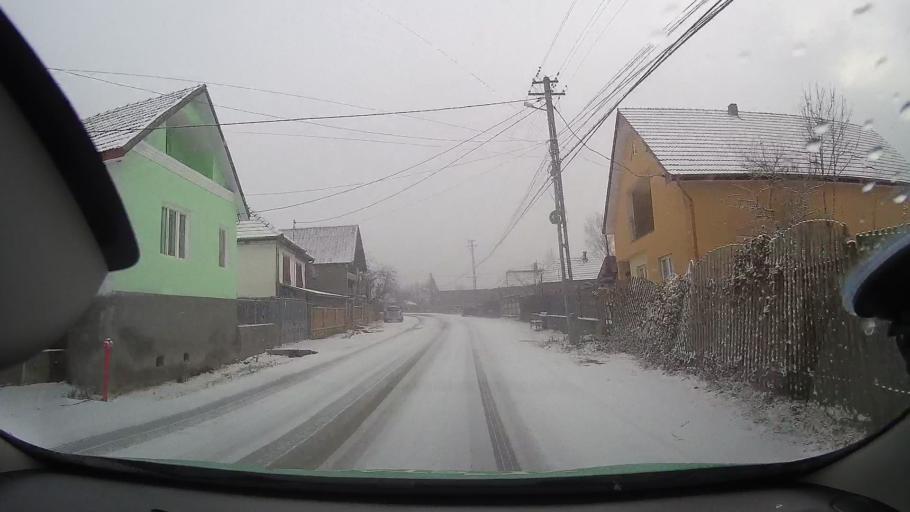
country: RO
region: Alba
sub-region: Comuna Livezile
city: Livezile
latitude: 46.3497
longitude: 23.6279
